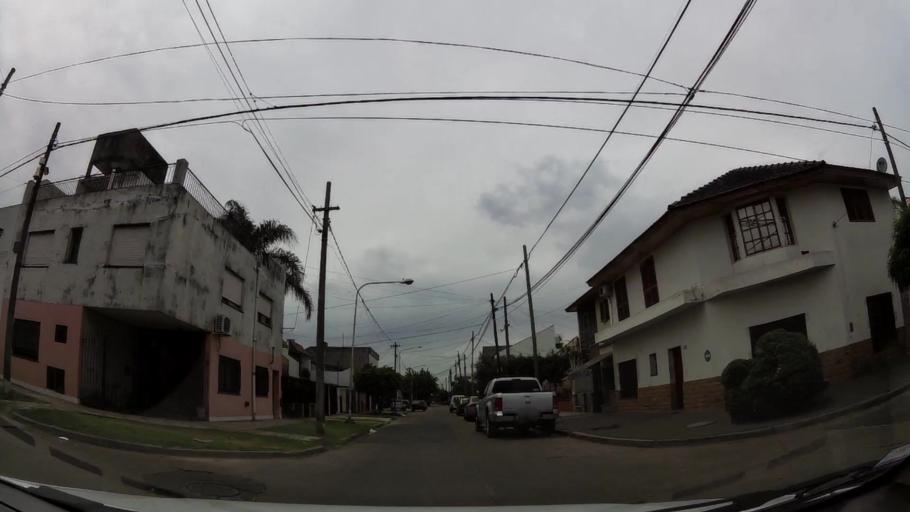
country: AR
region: Buenos Aires
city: San Justo
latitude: -34.6687
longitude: -58.5437
